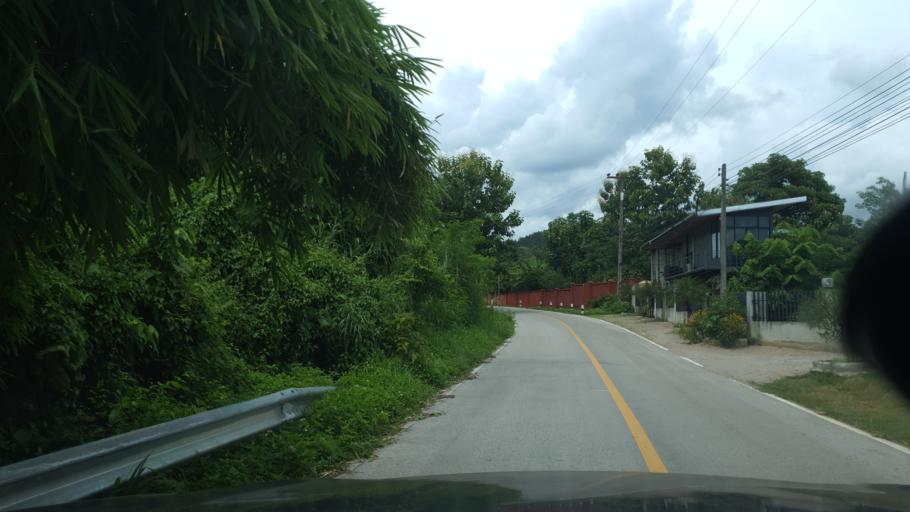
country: TH
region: Lampang
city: Hang Chat
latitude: 18.3972
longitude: 99.2644
